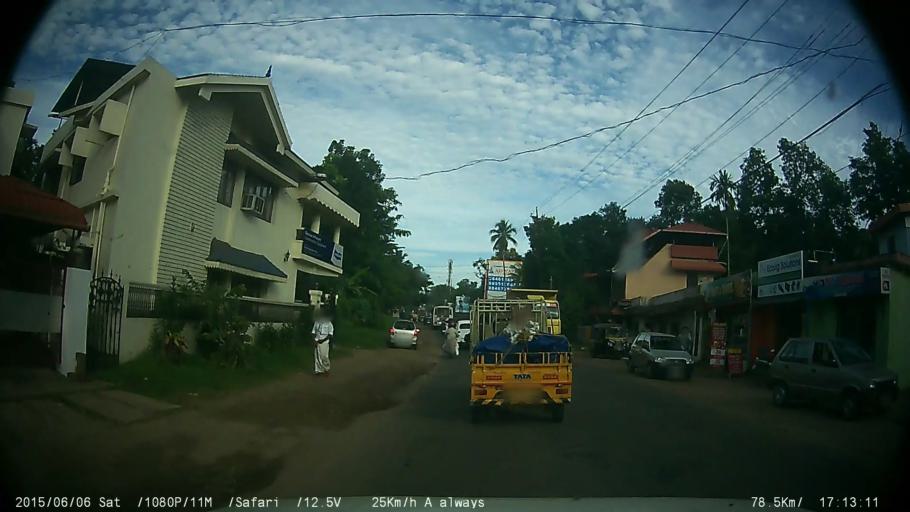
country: IN
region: Kerala
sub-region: Pattanamtitta
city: Tiruvalla
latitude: 9.4008
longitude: 76.5637
